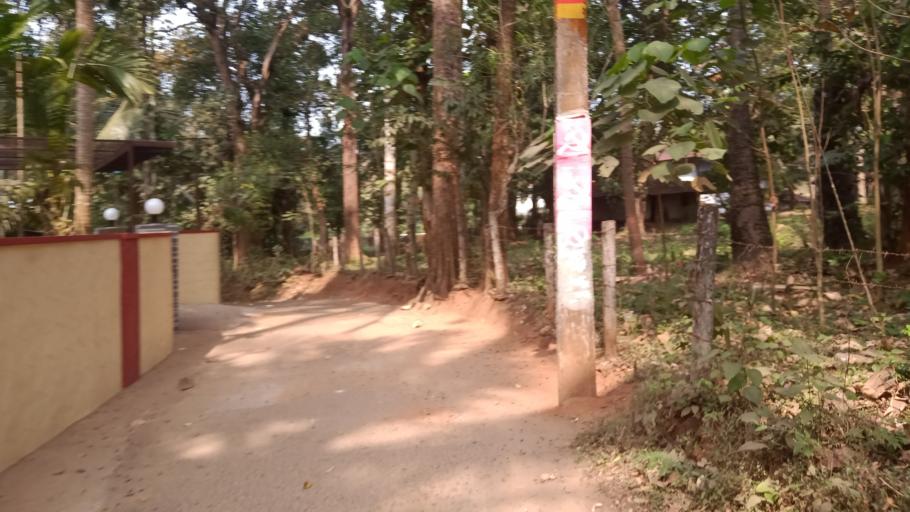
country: IN
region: Kerala
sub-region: Palakkad district
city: Cherpulassery
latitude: 10.8876
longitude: 76.3152
